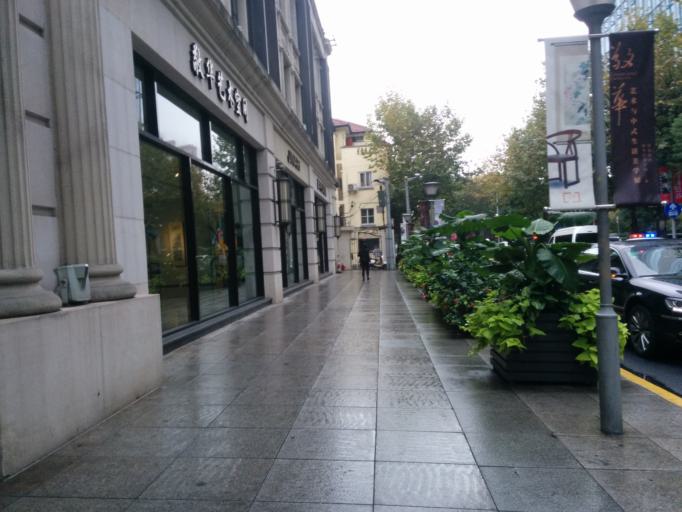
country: CN
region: Shanghai Shi
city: Shanghai
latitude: 31.2265
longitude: 121.4459
